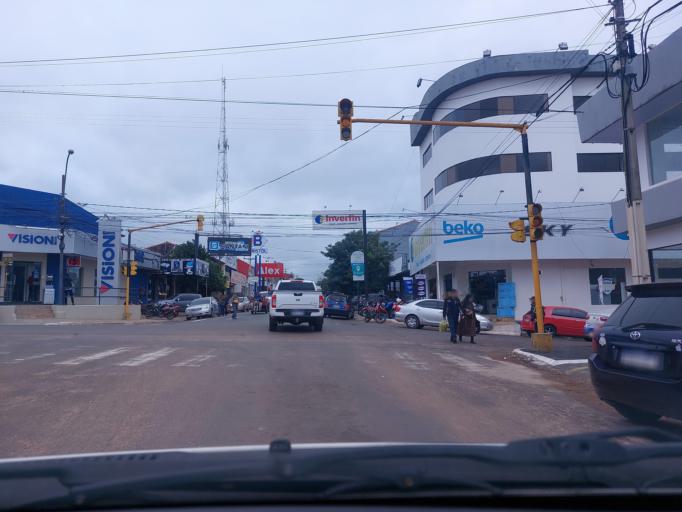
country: PY
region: San Pedro
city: Guayaybi
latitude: -24.6626
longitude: -56.4434
